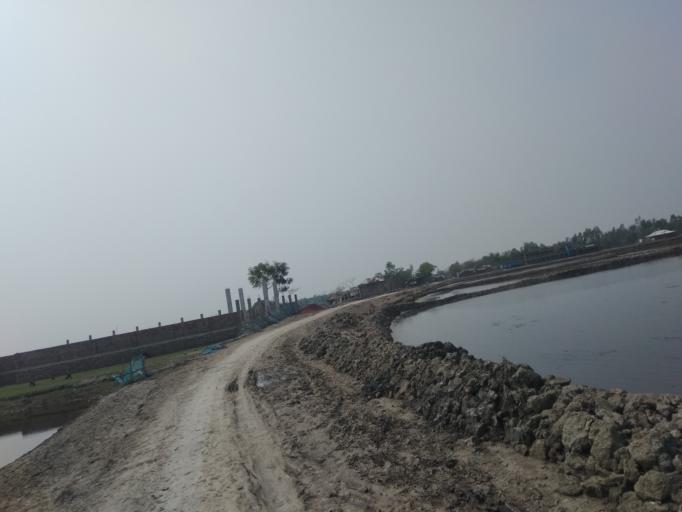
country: IN
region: West Bengal
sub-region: North 24 Parganas
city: Taki
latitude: 22.3476
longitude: 89.2223
